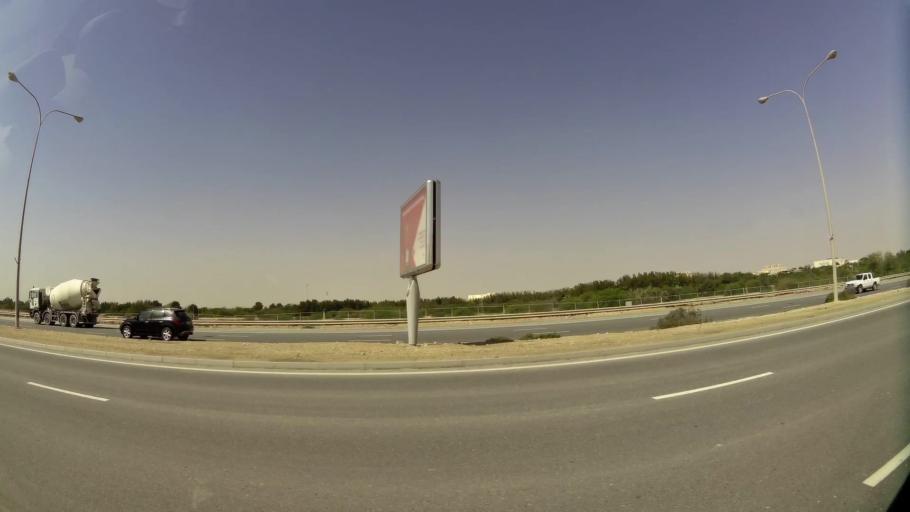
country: QA
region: Baladiyat ad Dawhah
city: Doha
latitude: 25.3707
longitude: 51.4974
